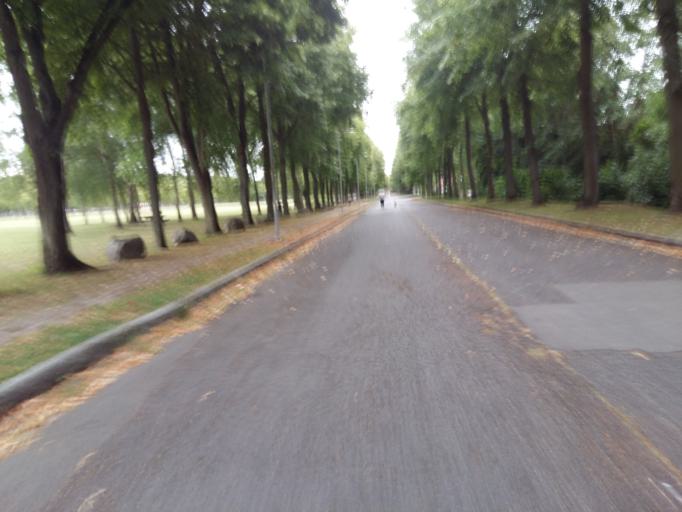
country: FR
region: Picardie
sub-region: Departement de la Somme
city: Amiens
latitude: 49.8981
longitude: 2.2764
